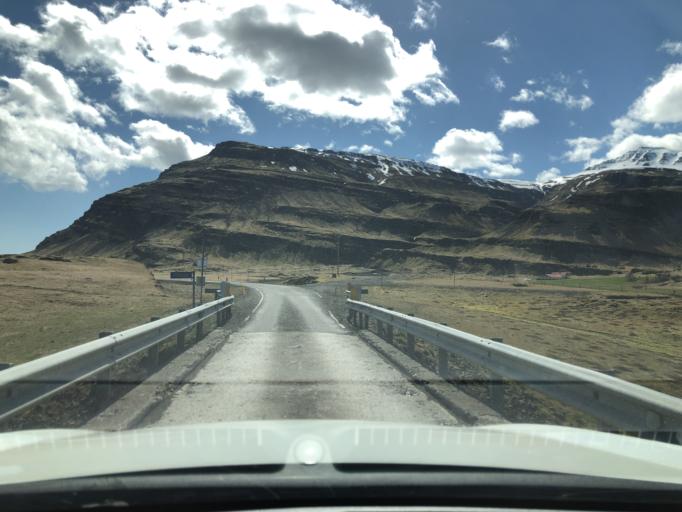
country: IS
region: East
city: Reydarfjoerdur
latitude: 64.5499
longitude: -14.6117
